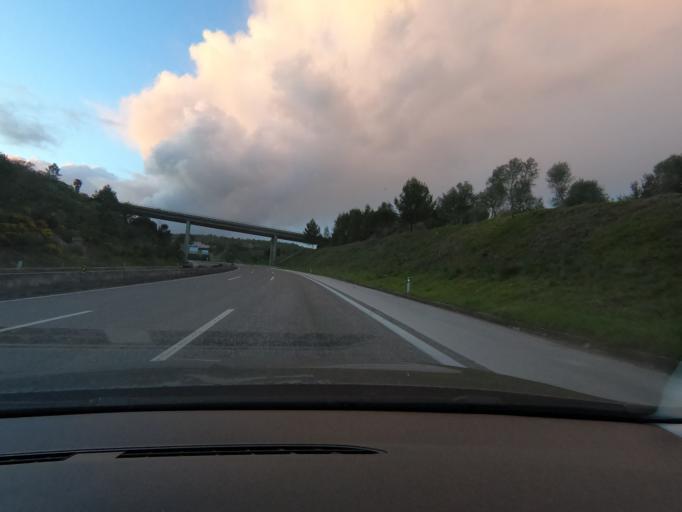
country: PT
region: Lisbon
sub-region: Vila Franca de Xira
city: Vialonga
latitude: 38.9017
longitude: -9.0561
